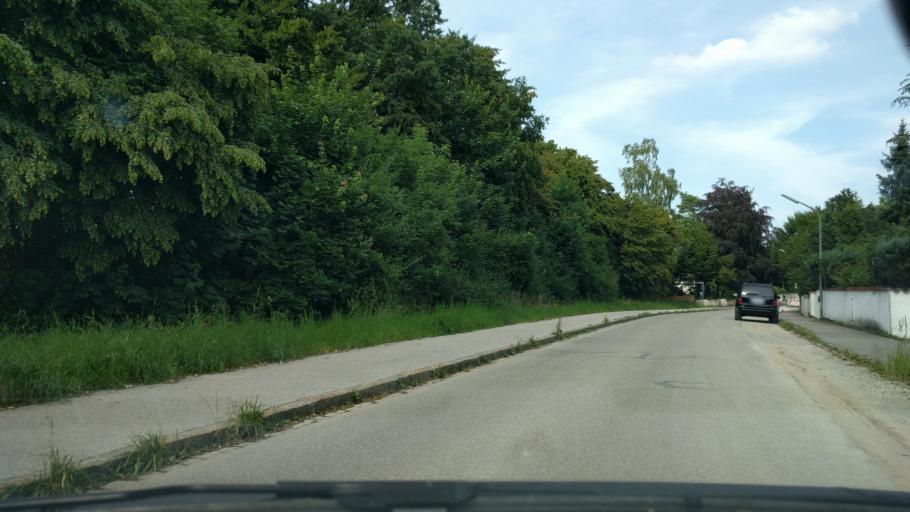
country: DE
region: Bavaria
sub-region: Upper Bavaria
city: Grunwald
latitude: 48.0454
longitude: 11.5332
